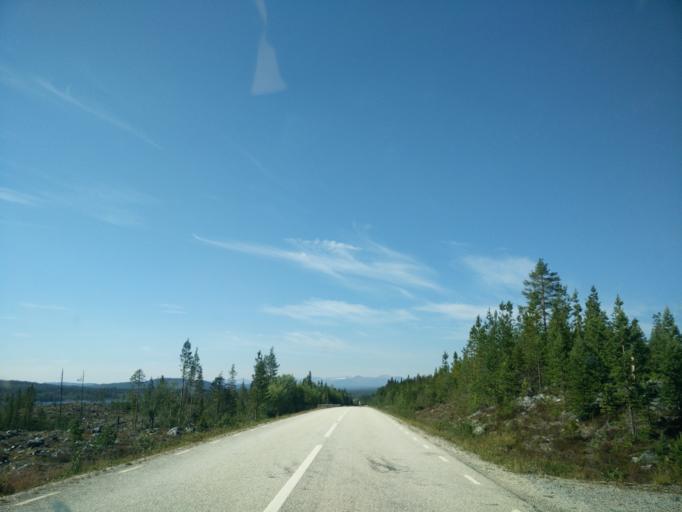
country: SE
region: Jaemtland
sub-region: Are Kommun
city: Jarpen
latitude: 62.8067
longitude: 13.5385
